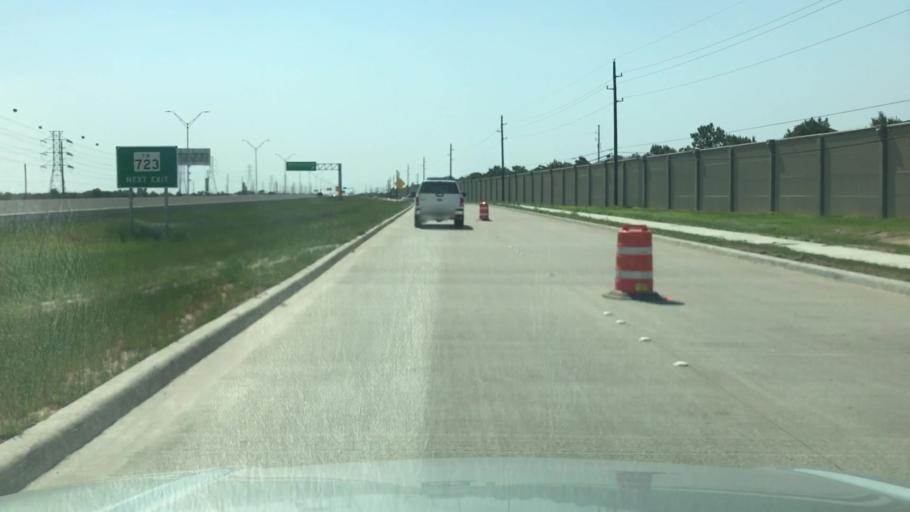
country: US
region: Texas
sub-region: Fort Bend County
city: Cinco Ranch
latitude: 29.6987
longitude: -95.7991
